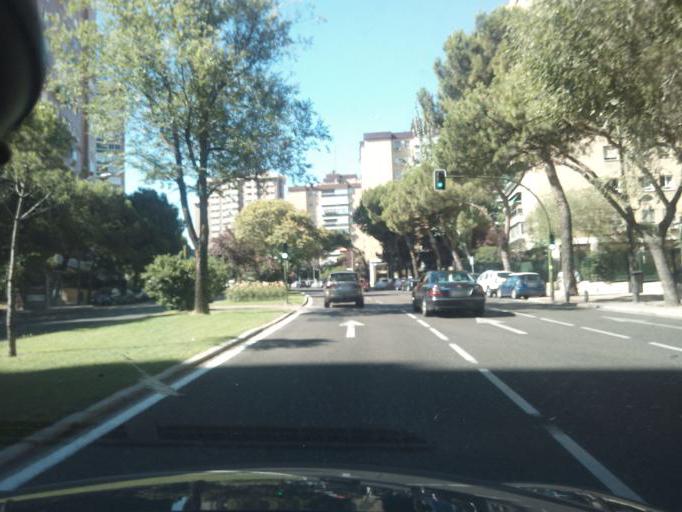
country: ES
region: Madrid
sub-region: Provincia de Madrid
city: Pinar de Chamartin
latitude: 40.4791
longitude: -3.6683
